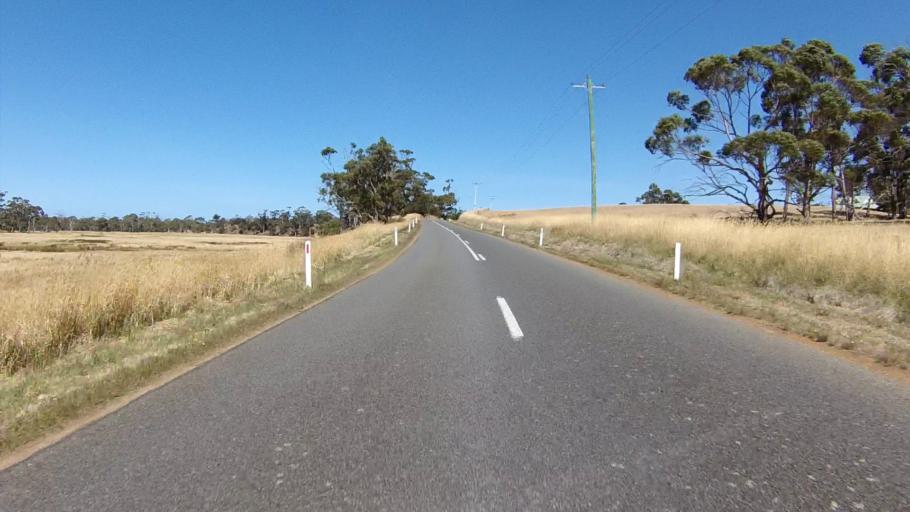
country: AU
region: Tasmania
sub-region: Sorell
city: Sorell
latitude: -42.2654
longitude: 148.0026
